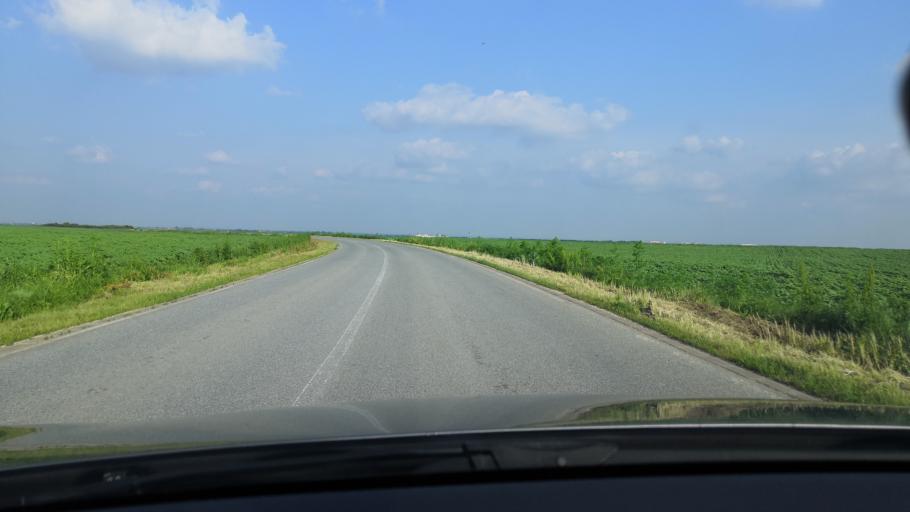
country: RS
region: Autonomna Pokrajina Vojvodina
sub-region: Sremski Okrug
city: Ingija
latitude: 45.0893
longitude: 20.0997
